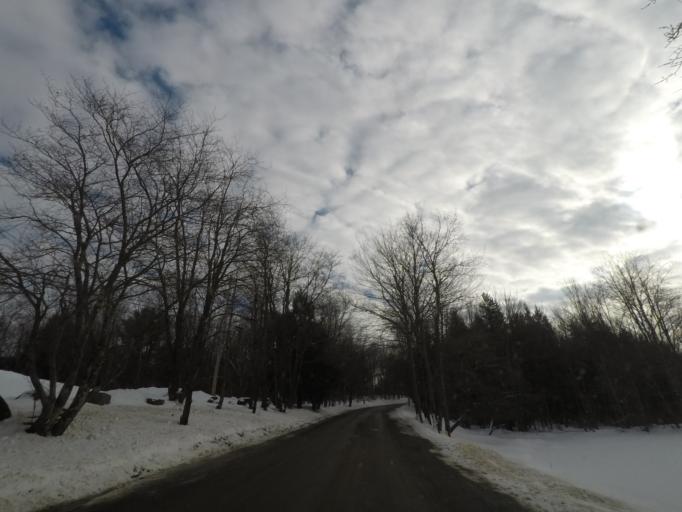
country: US
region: New York
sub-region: Rensselaer County
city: Averill Park
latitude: 42.6407
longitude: -73.4798
